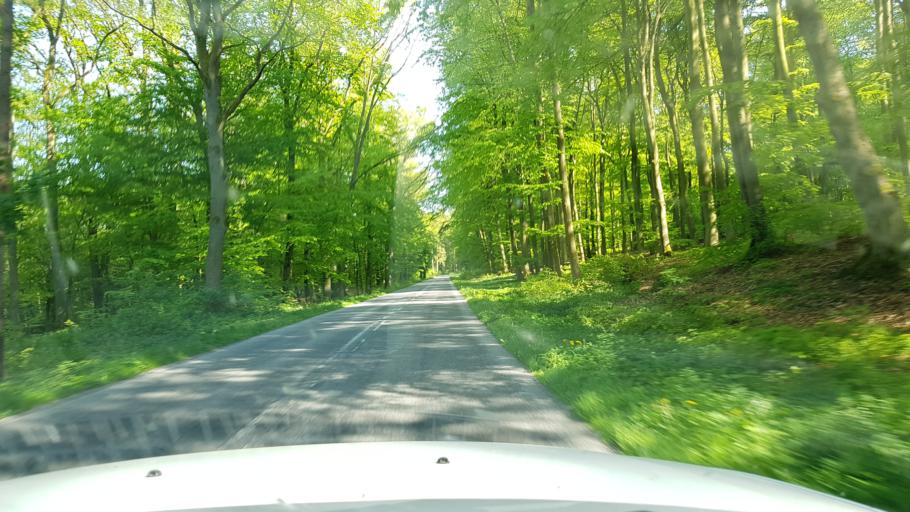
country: PL
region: West Pomeranian Voivodeship
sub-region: Powiat lobeski
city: Resko
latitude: 53.8388
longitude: 15.3776
